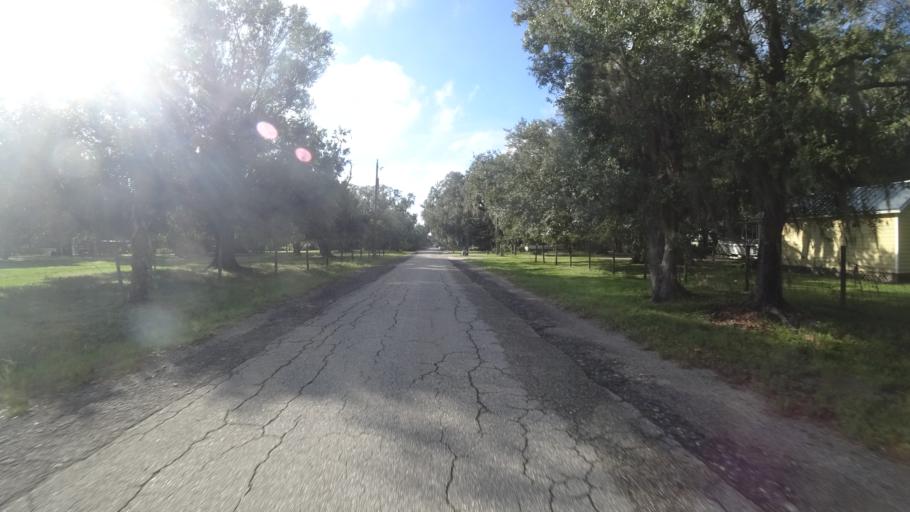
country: US
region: Florida
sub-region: Manatee County
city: Ellenton
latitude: 27.5730
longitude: -82.3924
